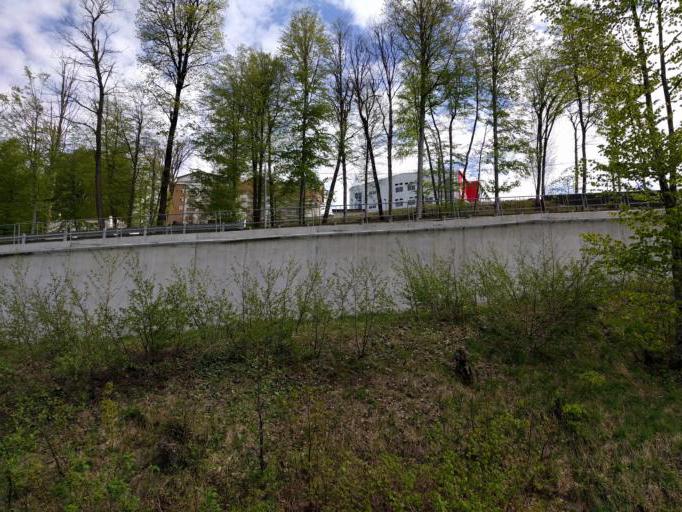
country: RU
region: Krasnodarskiy
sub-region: Sochi City
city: Krasnaya Polyana
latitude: 43.6623
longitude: 40.3132
